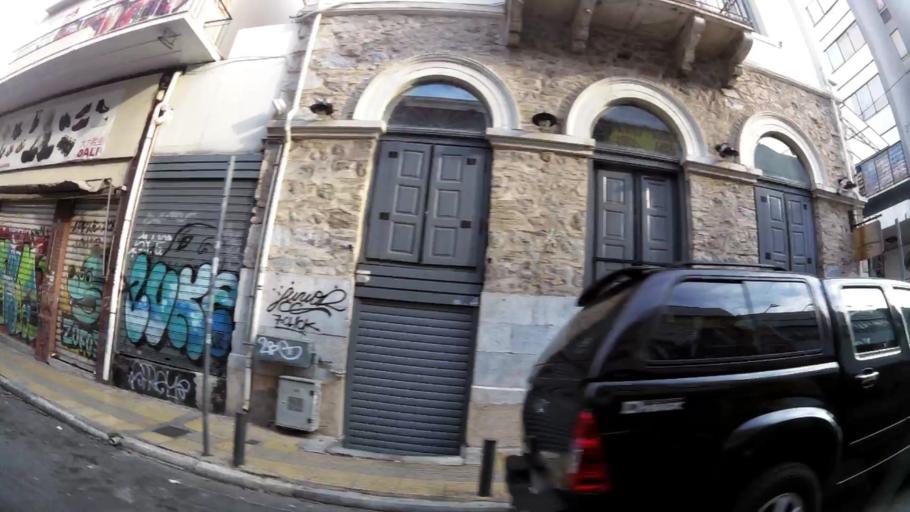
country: GR
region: Attica
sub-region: Nomarchia Athinas
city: Athens
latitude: 37.9801
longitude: 23.7256
